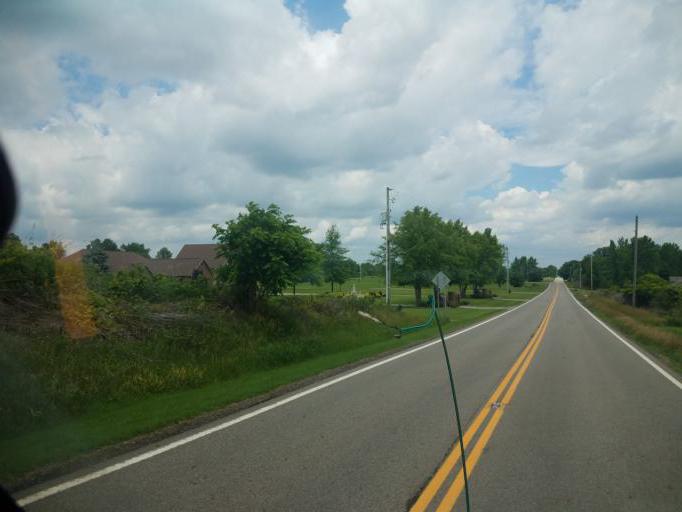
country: US
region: Ohio
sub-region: Huron County
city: Plymouth
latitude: 40.9745
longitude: -82.6741
